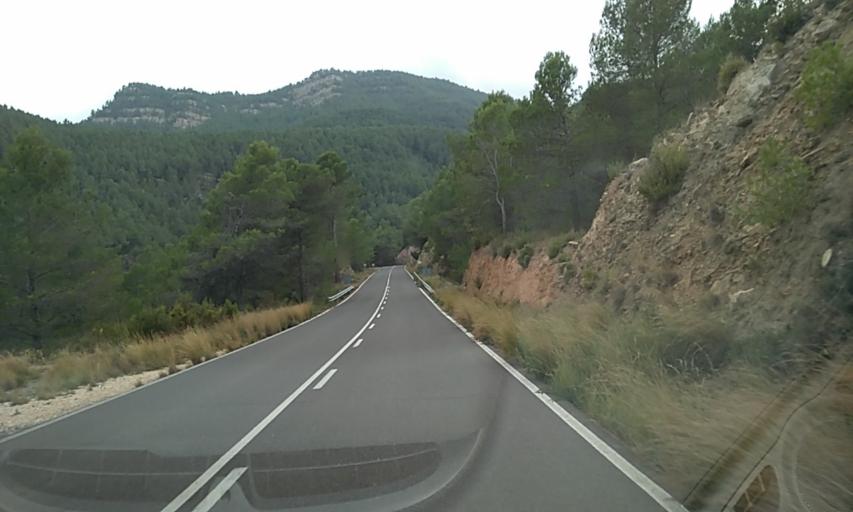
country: ES
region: Valencia
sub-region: Provincia de Castello
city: Puebla de Arenoso
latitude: 40.0960
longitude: -0.5728
